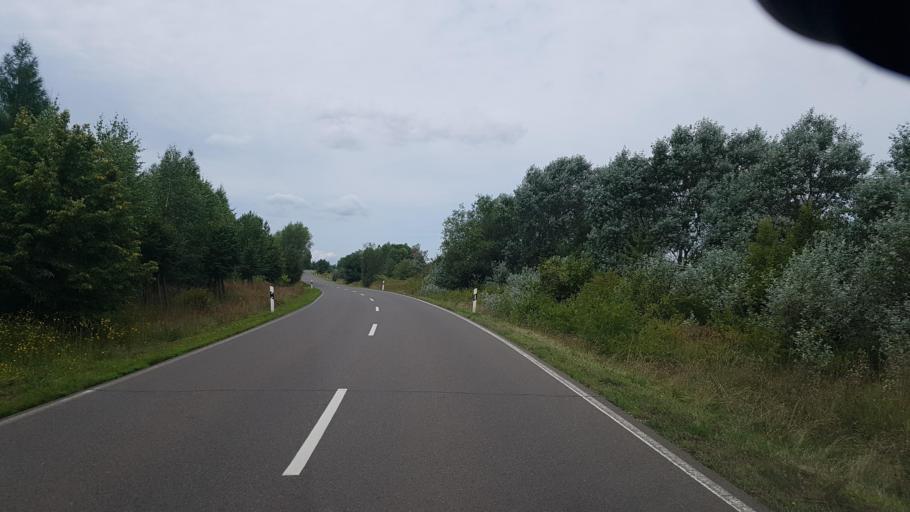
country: DE
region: Brandenburg
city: Spremberg
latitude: 51.5902
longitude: 14.3264
